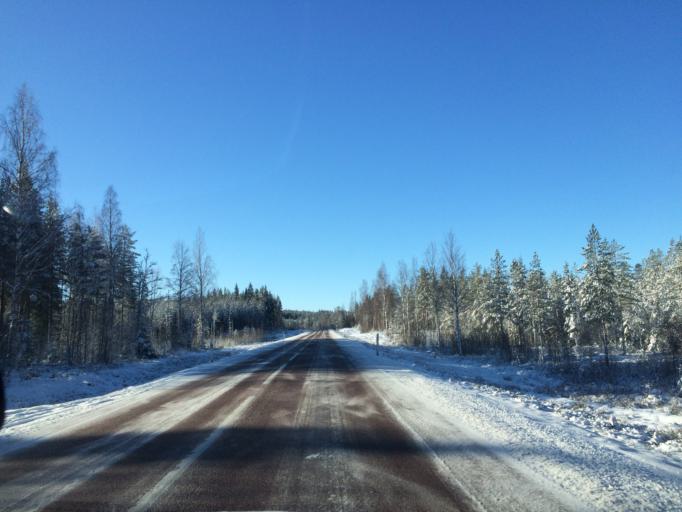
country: SE
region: Dalarna
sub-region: Mora Kommun
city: Mora
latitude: 60.8782
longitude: 14.3719
